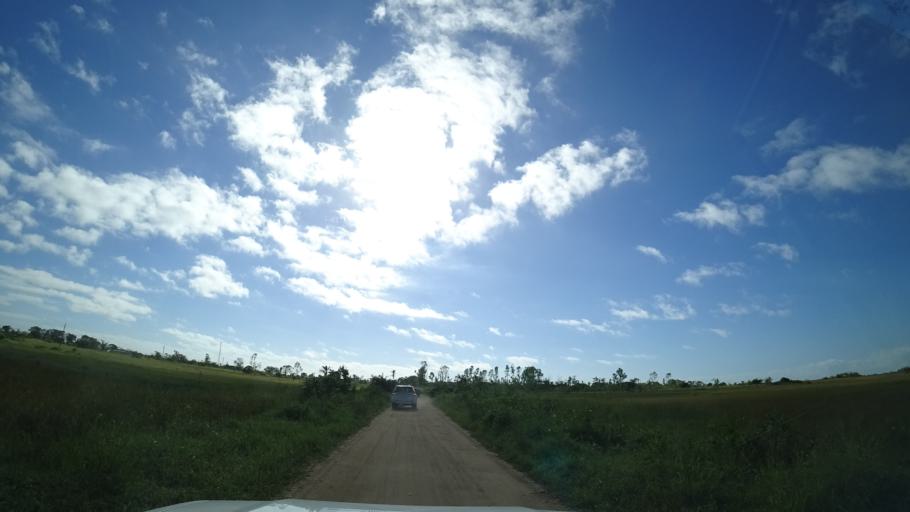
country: MZ
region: Sofala
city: Beira
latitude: -19.7199
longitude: 35.0008
